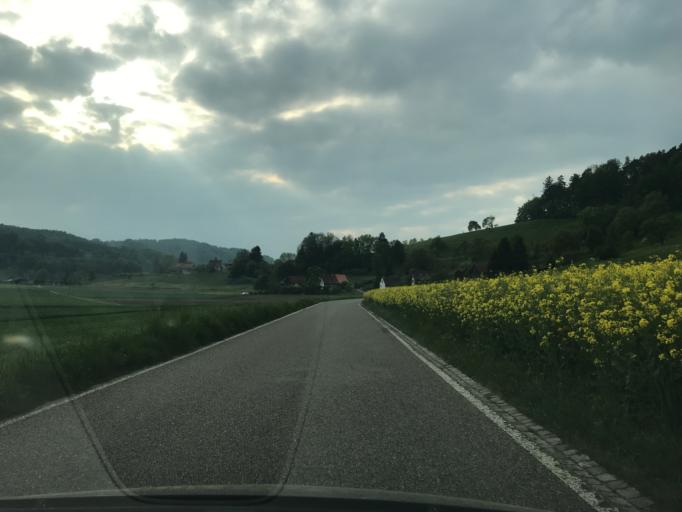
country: CH
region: Zurich
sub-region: Bezirk Winterthur
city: Wuelflingen (Kreis 6) / Oberfeld
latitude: 47.4948
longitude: 8.6850
